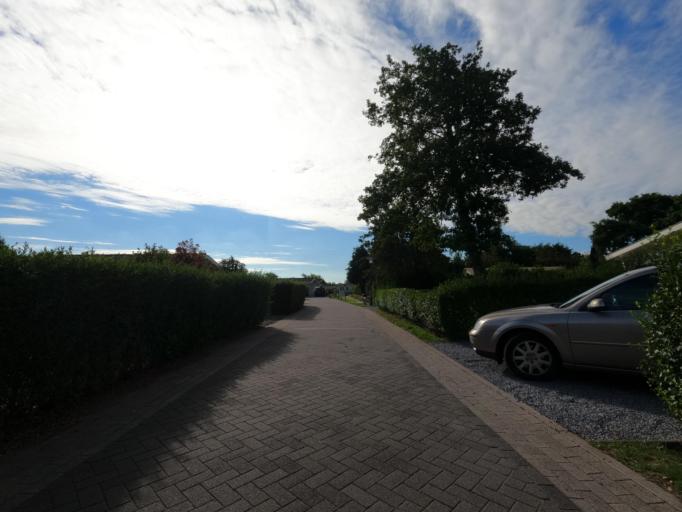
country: NL
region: South Holland
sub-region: Gemeente Noordwijkerhout
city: Noordwijkerhout
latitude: 52.2708
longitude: 4.4719
